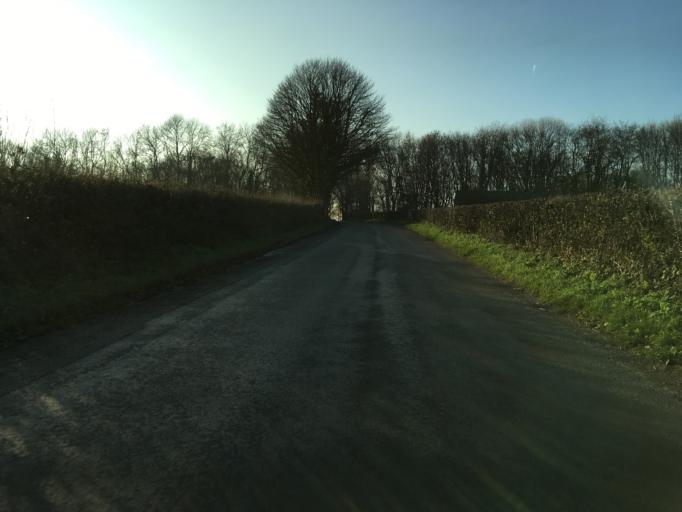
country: GB
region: England
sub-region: South Gloucestershire
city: Horton
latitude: 51.5550
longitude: -2.3368
